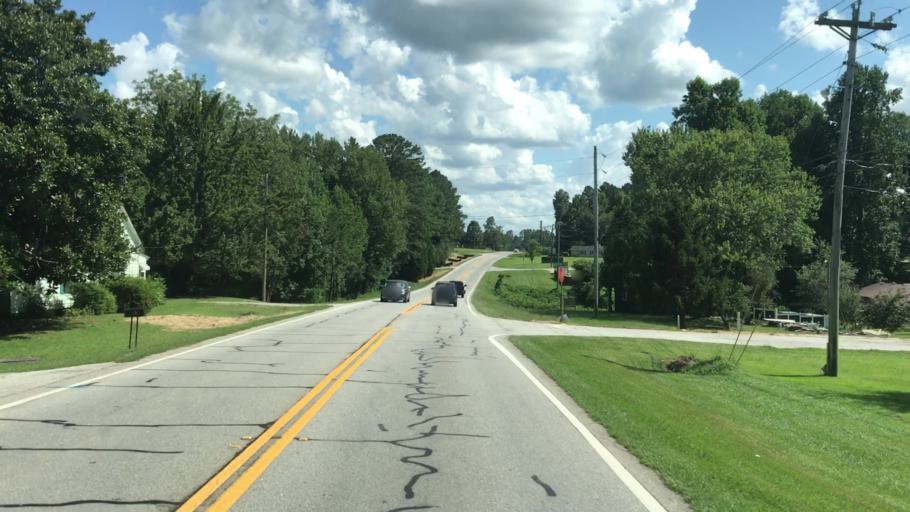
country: US
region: Georgia
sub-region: Walton County
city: Walnut Grove
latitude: 33.7636
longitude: -83.8512
